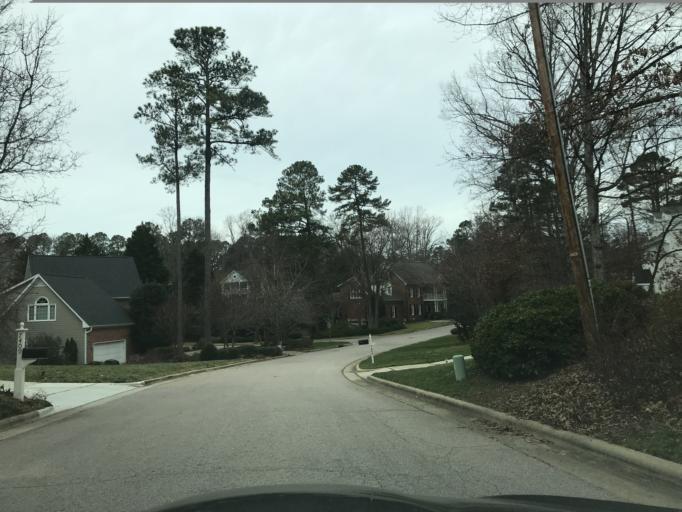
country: US
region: North Carolina
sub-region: Wake County
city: West Raleigh
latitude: 35.8823
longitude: -78.6077
